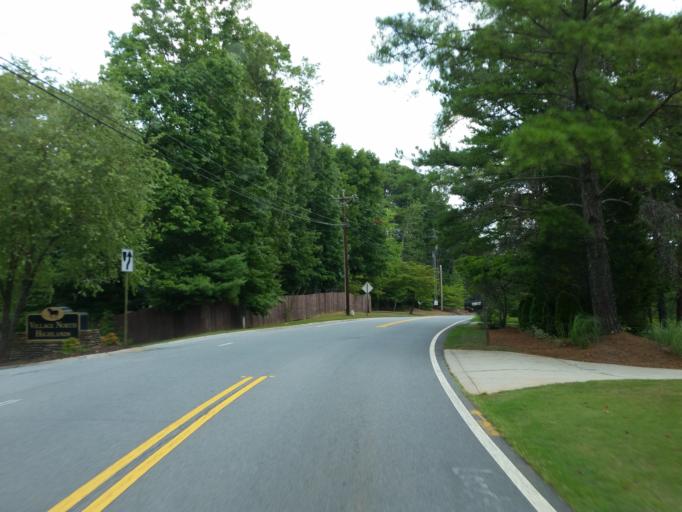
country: US
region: Georgia
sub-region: Fulton County
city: Roswell
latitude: 34.0444
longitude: -84.4351
